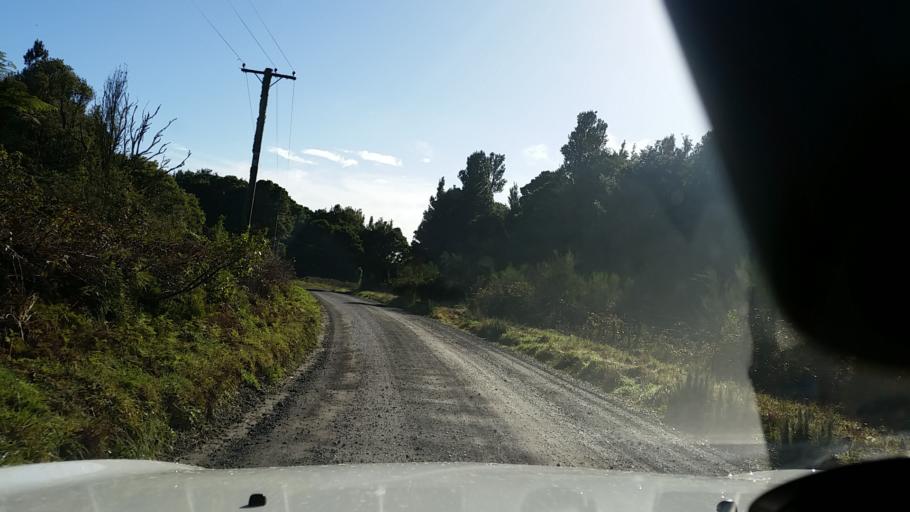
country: NZ
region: Bay of Plenty
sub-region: Kawerau District
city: Kawerau
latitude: -38.0134
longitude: 176.4900
